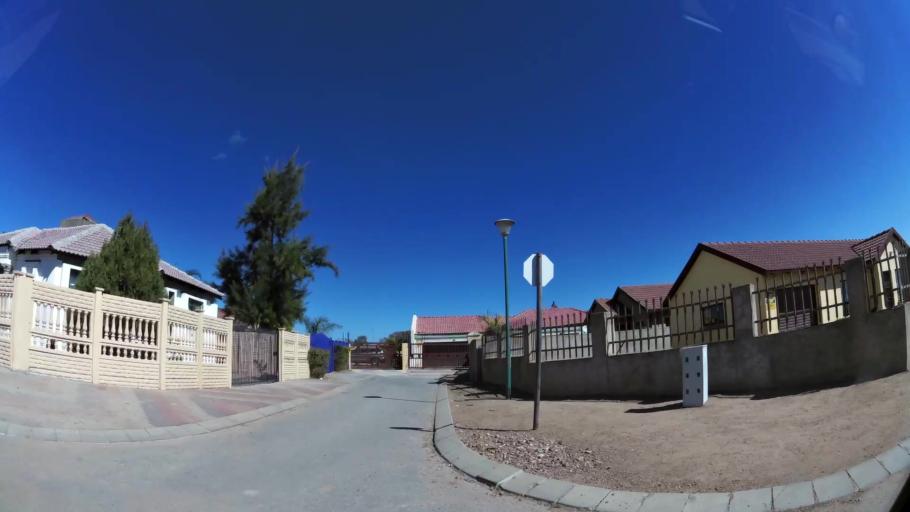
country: ZA
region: Limpopo
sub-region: Capricorn District Municipality
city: Polokwane
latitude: -23.8668
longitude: 29.4242
